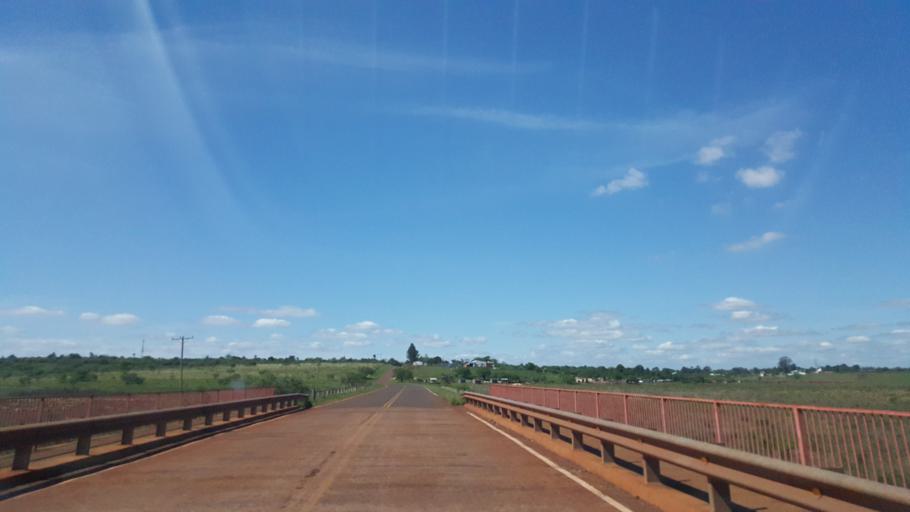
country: AR
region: Misiones
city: Garupa
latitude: -27.4930
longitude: -55.8375
